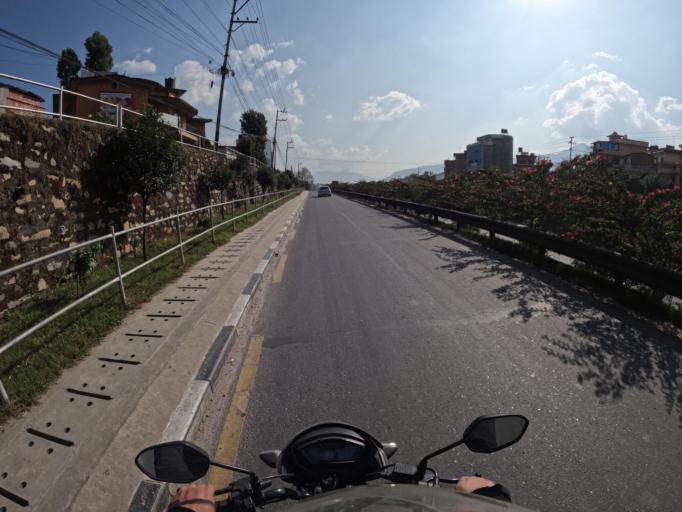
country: NP
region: Central Region
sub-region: Bagmati Zone
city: Patan
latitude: 27.6803
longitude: 85.3025
